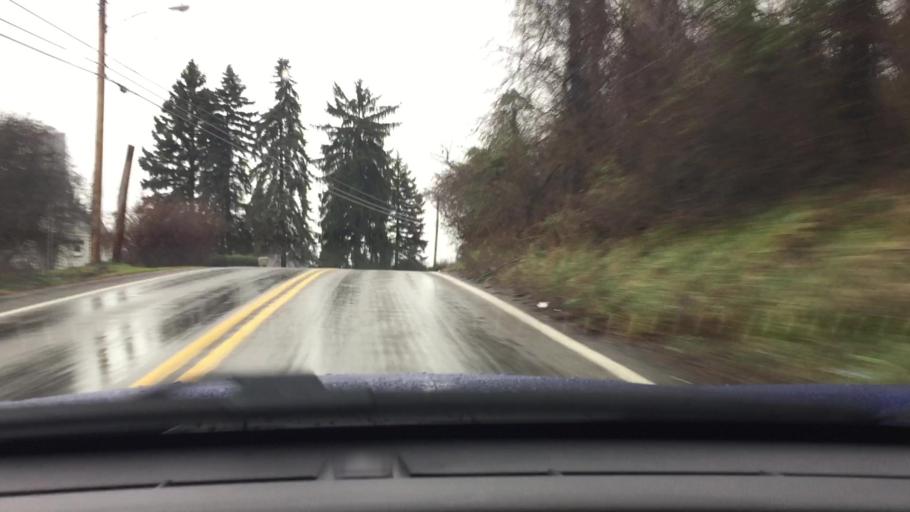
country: US
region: Pennsylvania
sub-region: Allegheny County
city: Jefferson Hills
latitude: 40.3083
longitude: -79.9173
